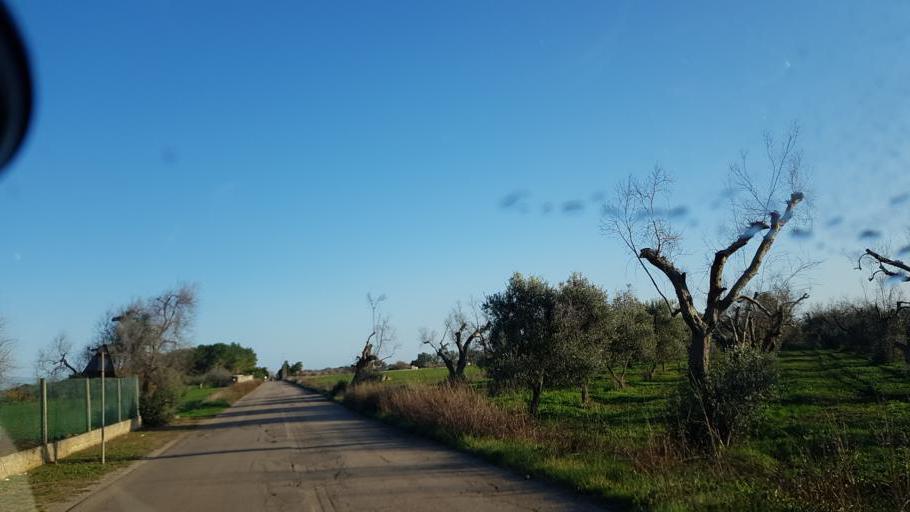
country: IT
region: Apulia
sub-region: Provincia di Brindisi
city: Torchiarolo
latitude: 40.5071
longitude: 18.0955
